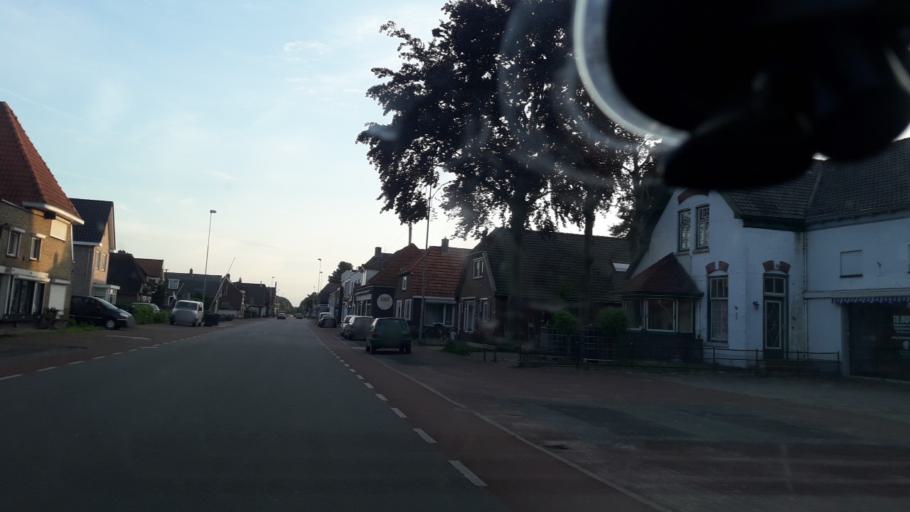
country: NL
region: Gelderland
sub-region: Gemeente Oldebroek
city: Oldebroek
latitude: 52.4492
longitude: 5.9024
